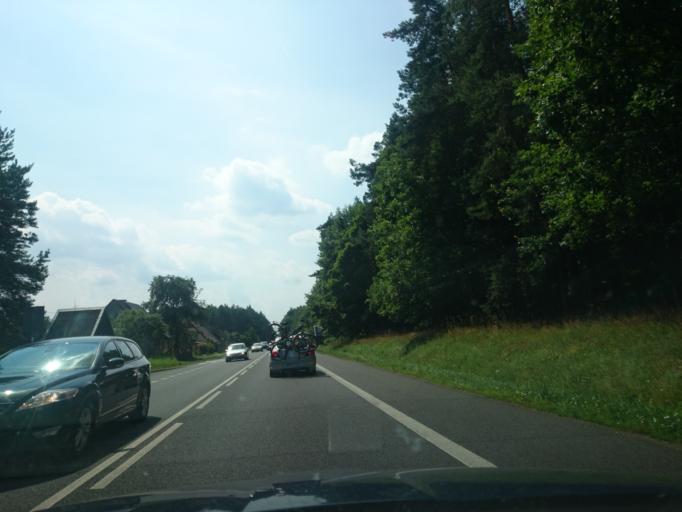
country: PL
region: West Pomeranian Voivodeship
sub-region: Powiat goleniowski
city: Przybiernow
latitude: 53.7364
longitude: 14.7751
